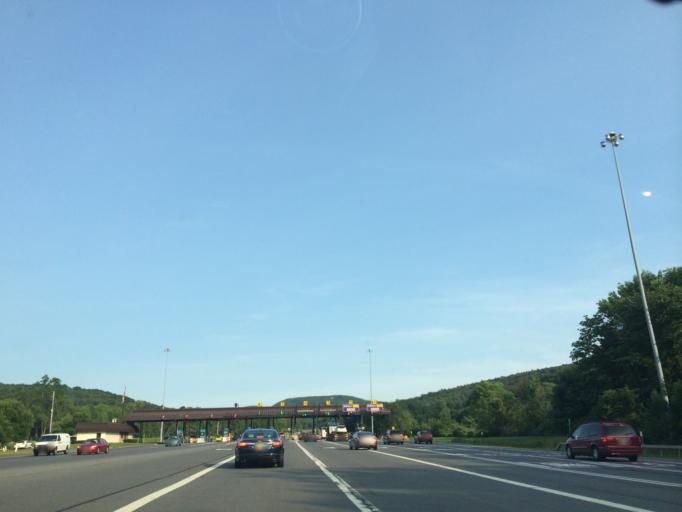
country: US
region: New York
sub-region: Columbia County
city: Chatham
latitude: 42.3993
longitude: -73.5065
